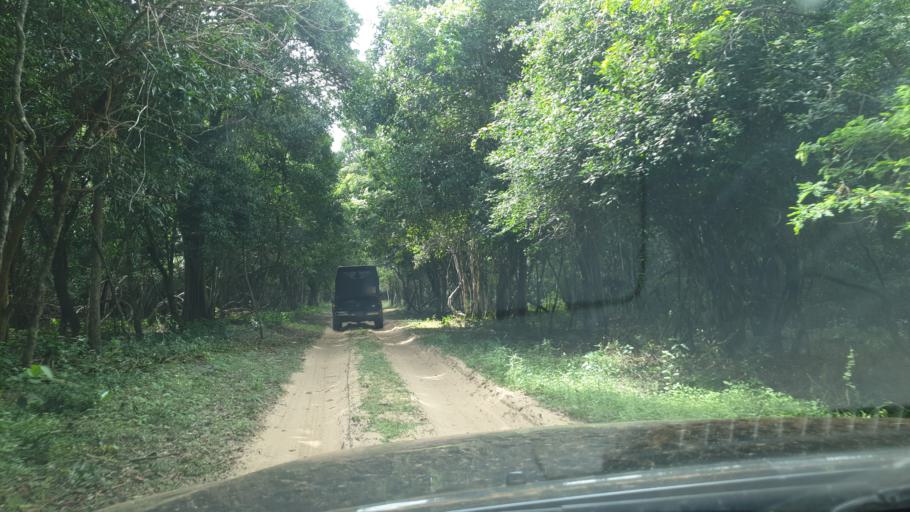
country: LK
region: North Western
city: Puttalam
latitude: 8.4123
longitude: 79.9890
